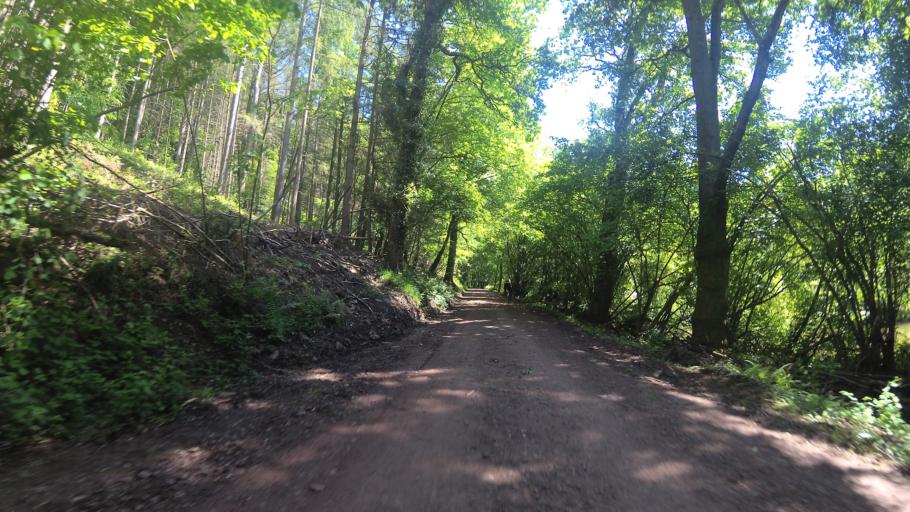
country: DE
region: Saarland
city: Mettlach
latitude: 49.4923
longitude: 6.5600
